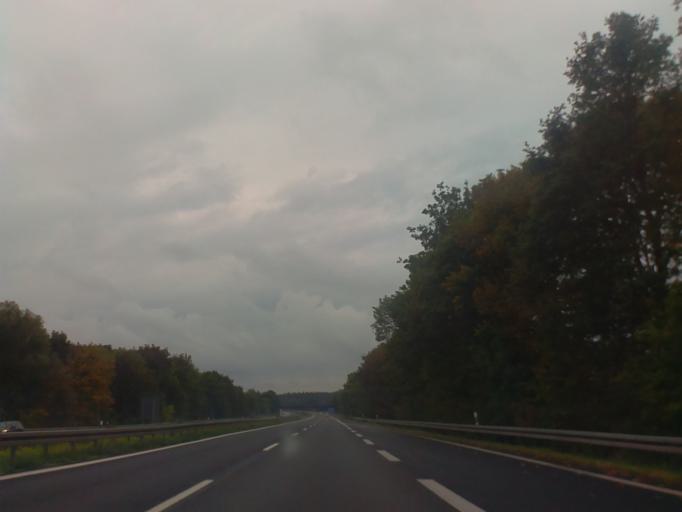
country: DE
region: Bavaria
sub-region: Regierungsbezirk Unterfranken
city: Alzenau in Unterfranken
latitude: 50.0835
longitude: 9.0357
